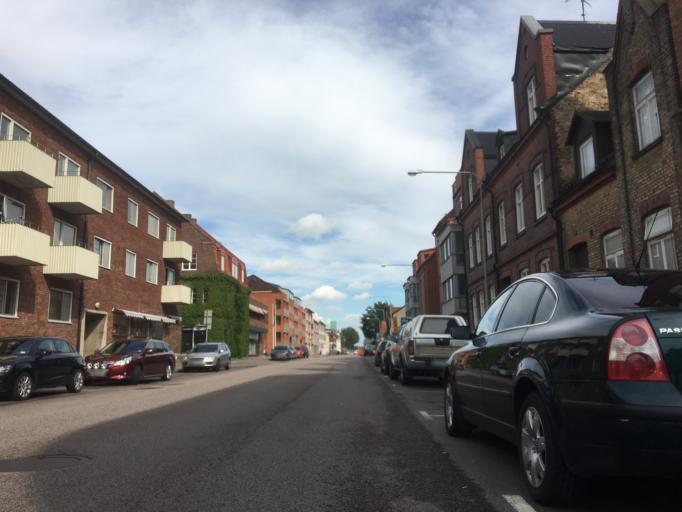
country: SE
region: Skane
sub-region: Landskrona
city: Landskrona
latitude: 55.8741
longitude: 12.8434
